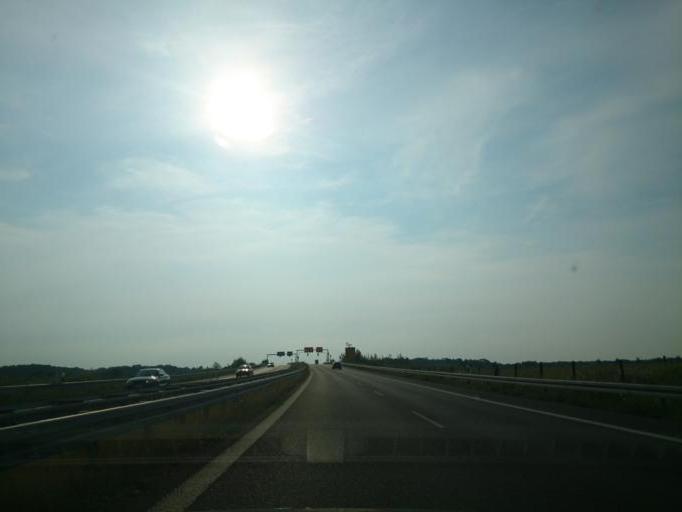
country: DE
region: Berlin
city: Lichtenrade
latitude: 52.3669
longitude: 13.4309
